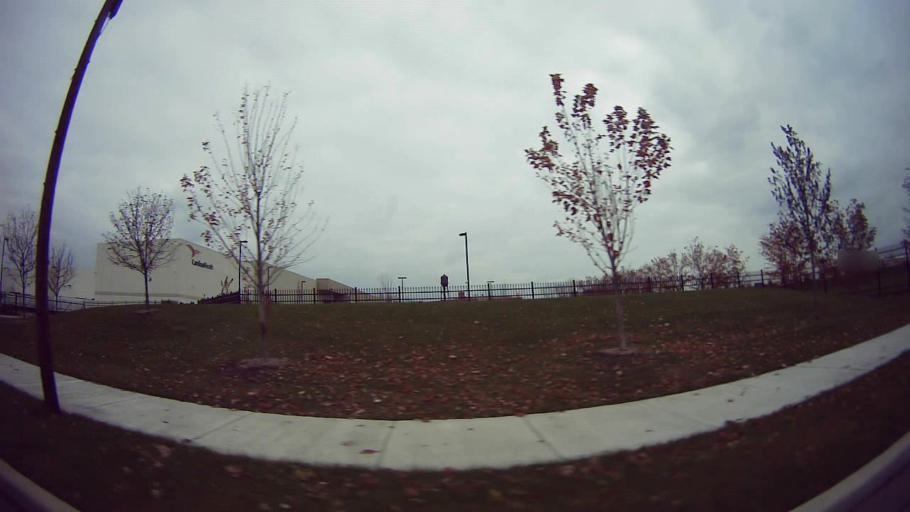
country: US
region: Michigan
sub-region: Wayne County
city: Detroit
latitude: 42.3577
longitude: -83.0869
